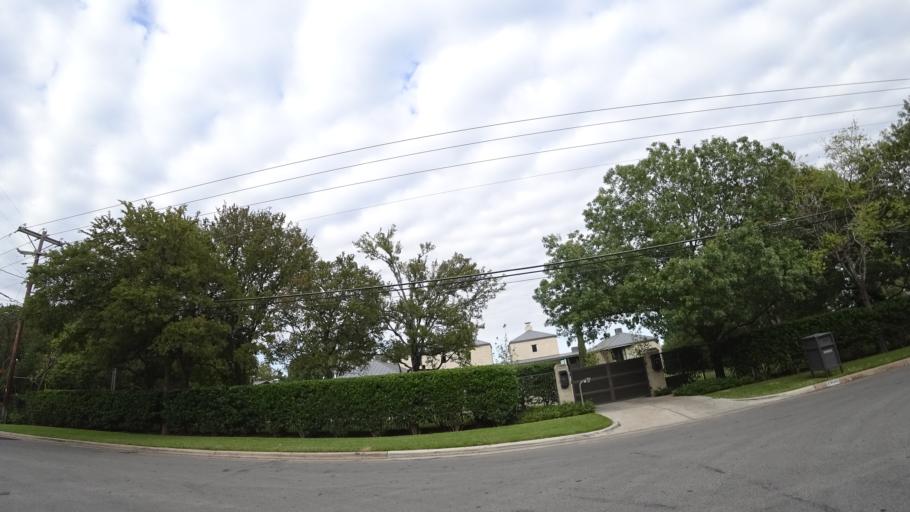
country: US
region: Texas
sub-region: Travis County
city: Rollingwood
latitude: 30.2815
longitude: -97.7840
